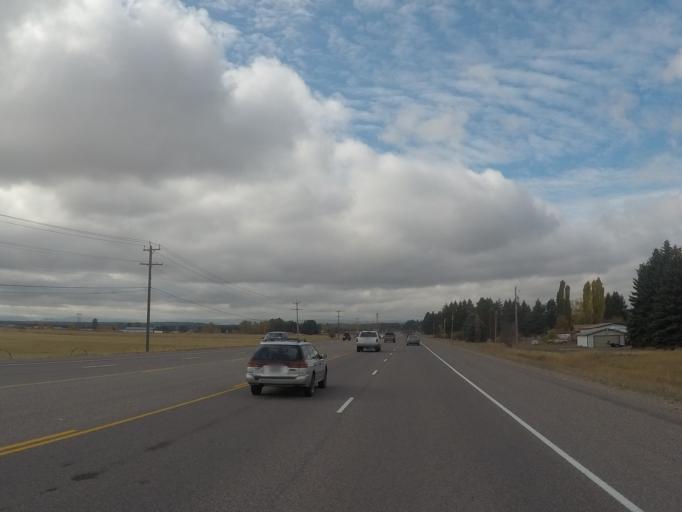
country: US
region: Montana
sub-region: Flathead County
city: Columbia Falls
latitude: 48.3708
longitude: -114.2250
